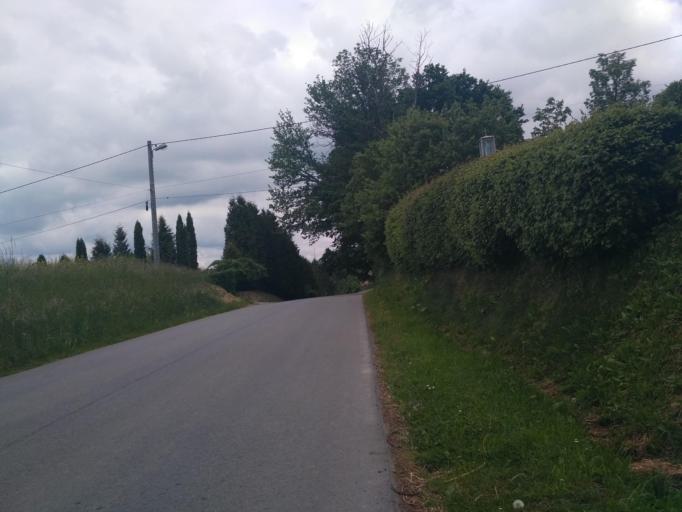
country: PL
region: Subcarpathian Voivodeship
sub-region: Powiat jasielski
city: Tarnowiec
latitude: 49.7144
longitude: 21.5818
